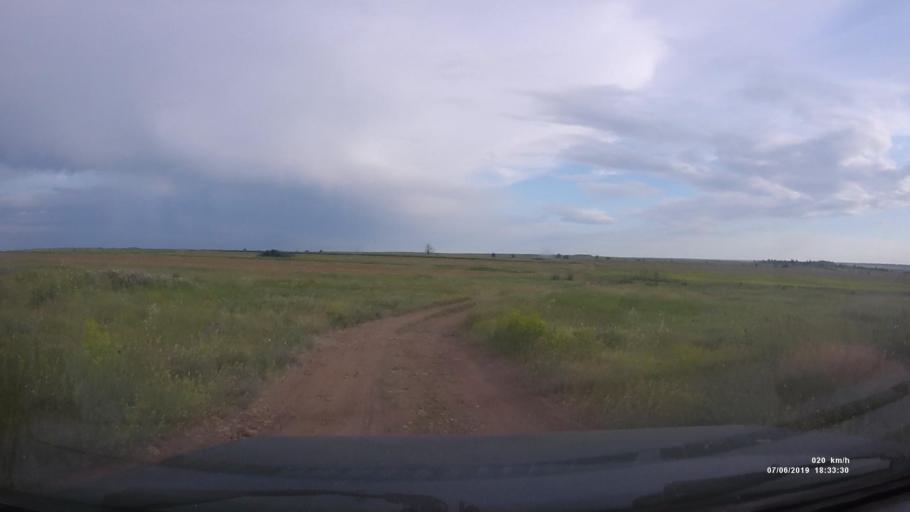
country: RU
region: Rostov
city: Staraya Stanitsa
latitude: 48.2613
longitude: 40.3626
